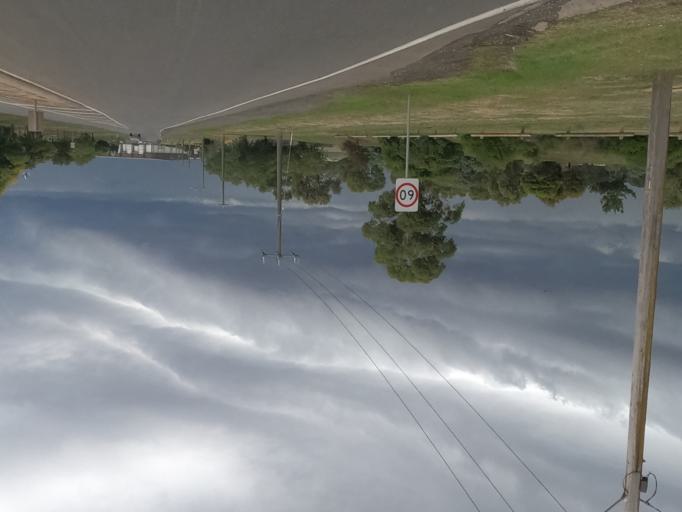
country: AU
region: Victoria
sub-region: Ballarat North
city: Lake Wendouree
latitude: -37.5209
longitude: 143.8255
